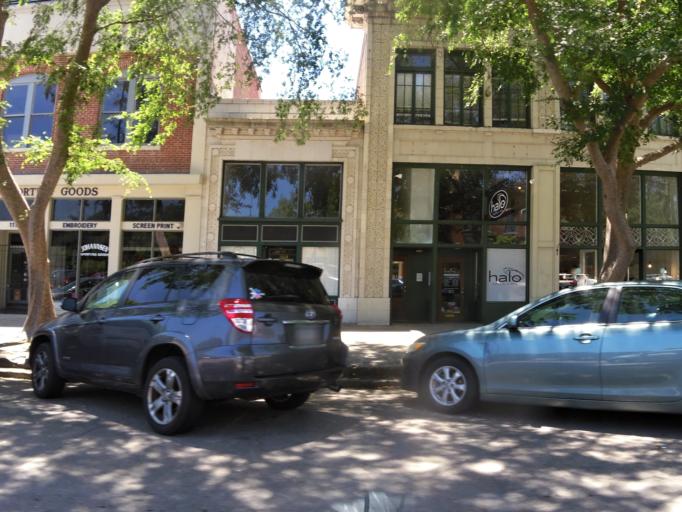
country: US
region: Georgia
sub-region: Richmond County
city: Augusta
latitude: 33.4773
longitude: -81.9717
